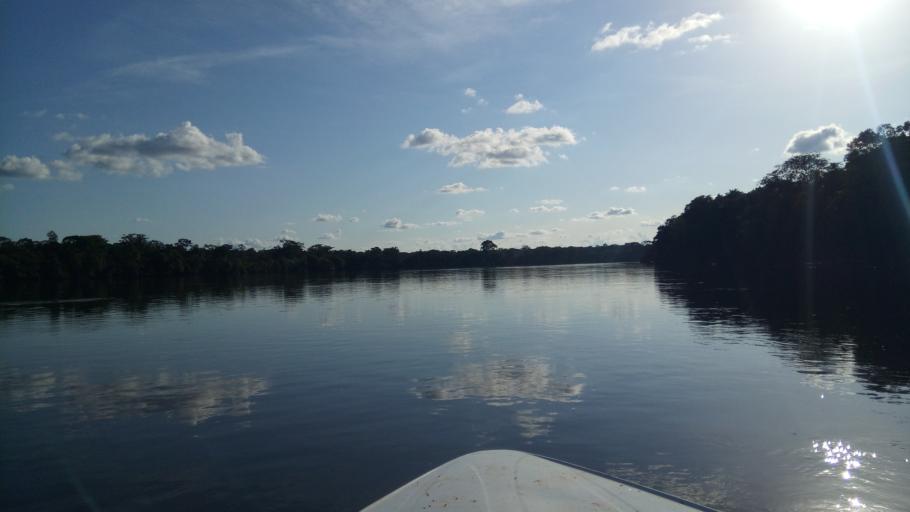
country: CD
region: Eastern Province
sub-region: Sous-Region de la Tshopo
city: Yangambi
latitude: 0.2338
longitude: 24.1040
